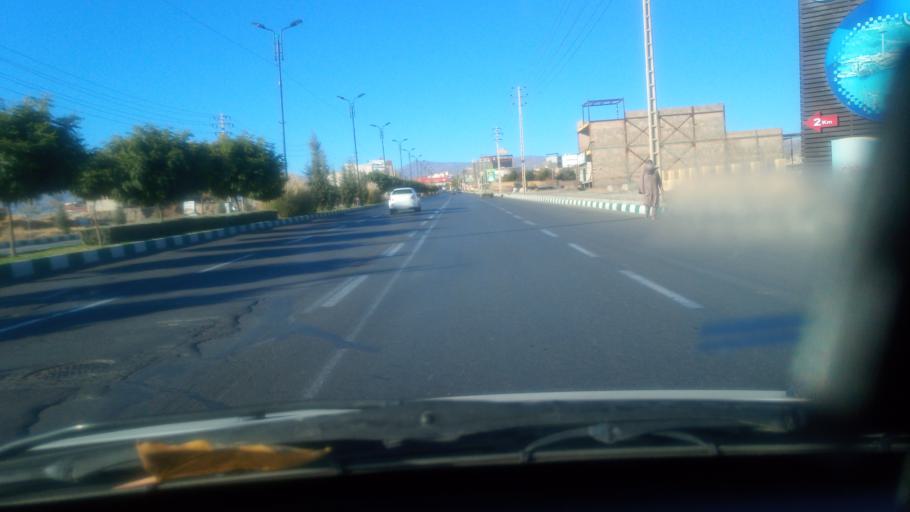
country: IR
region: Razavi Khorasan
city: Torqabeh
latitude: 36.3166
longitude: 59.3828
